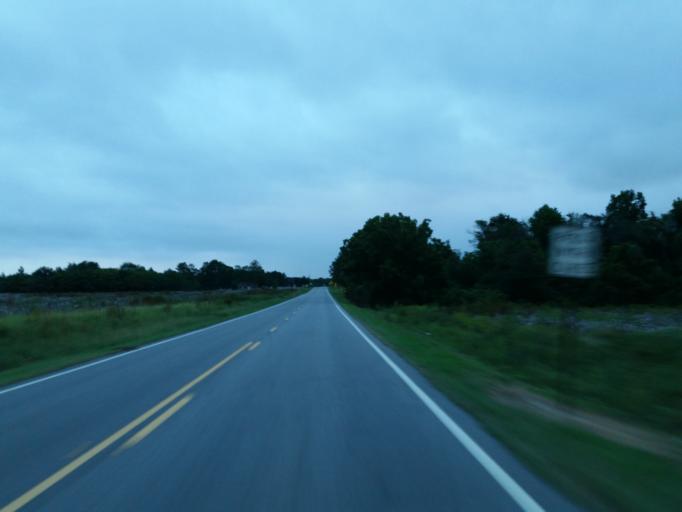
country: US
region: Georgia
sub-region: Crisp County
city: Cordele
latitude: 31.8482
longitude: -83.7446
